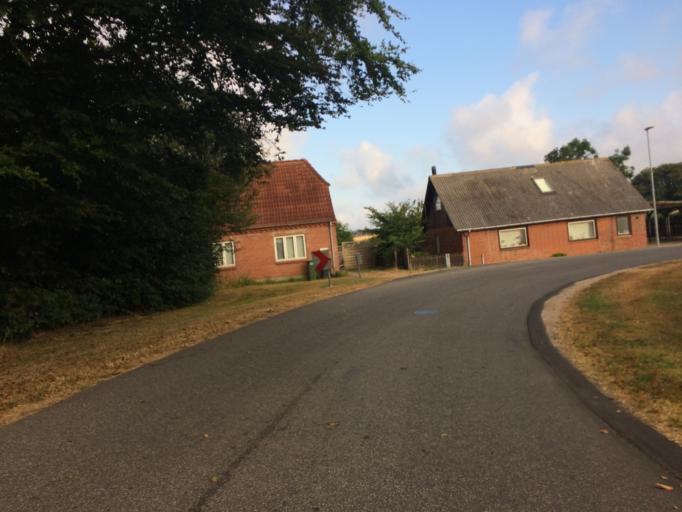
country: DK
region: Central Jutland
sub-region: Holstebro Kommune
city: Vinderup
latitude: 56.5959
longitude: 8.7314
